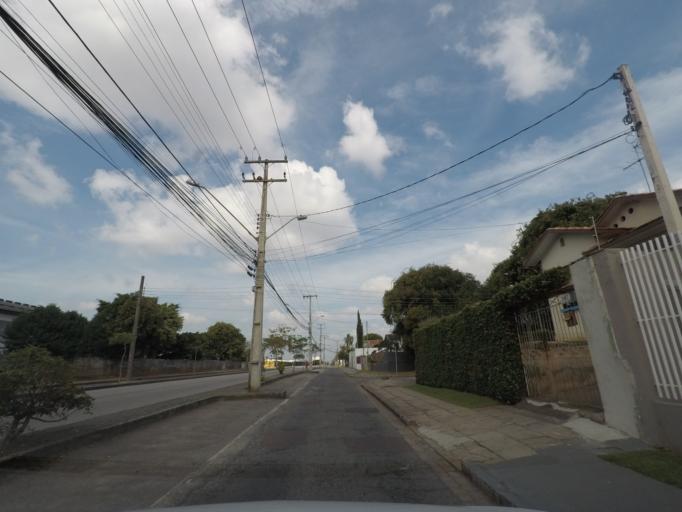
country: BR
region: Parana
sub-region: Pinhais
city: Pinhais
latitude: -25.4495
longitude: -49.2160
